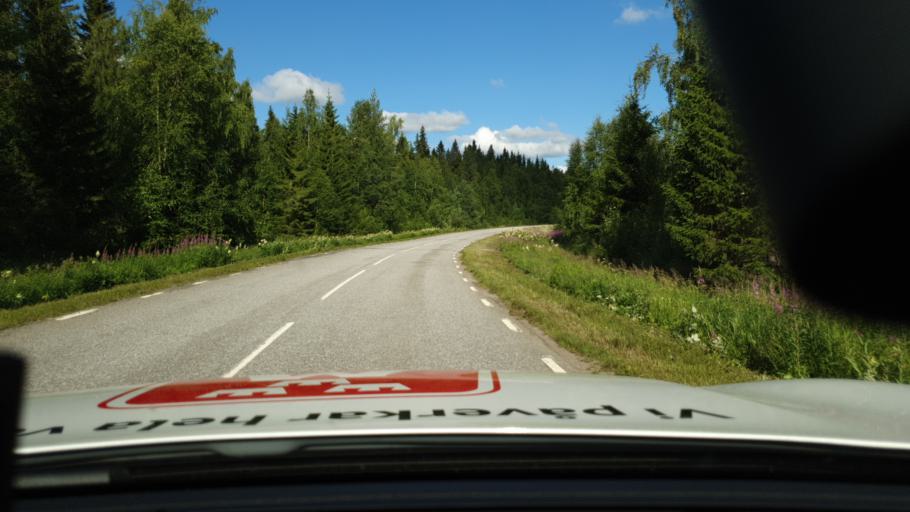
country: SE
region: Norrbotten
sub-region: Lulea Kommun
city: Ranea
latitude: 65.8814
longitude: 22.2059
